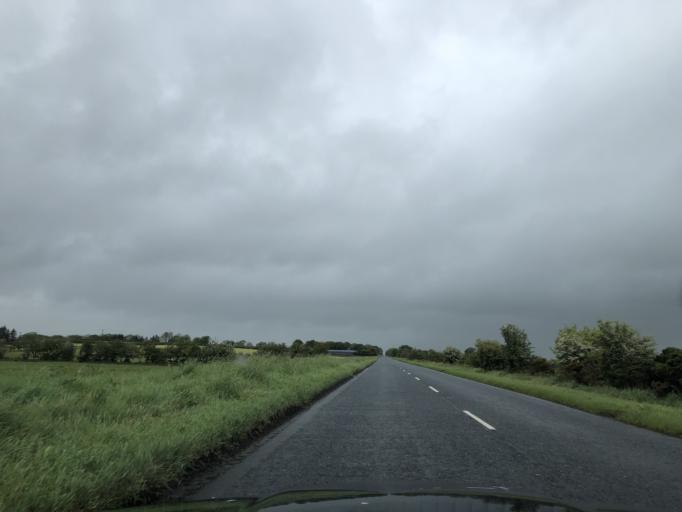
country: GB
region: Northern Ireland
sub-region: Moyle District
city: Ballycastle
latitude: 55.1731
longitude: -6.3411
